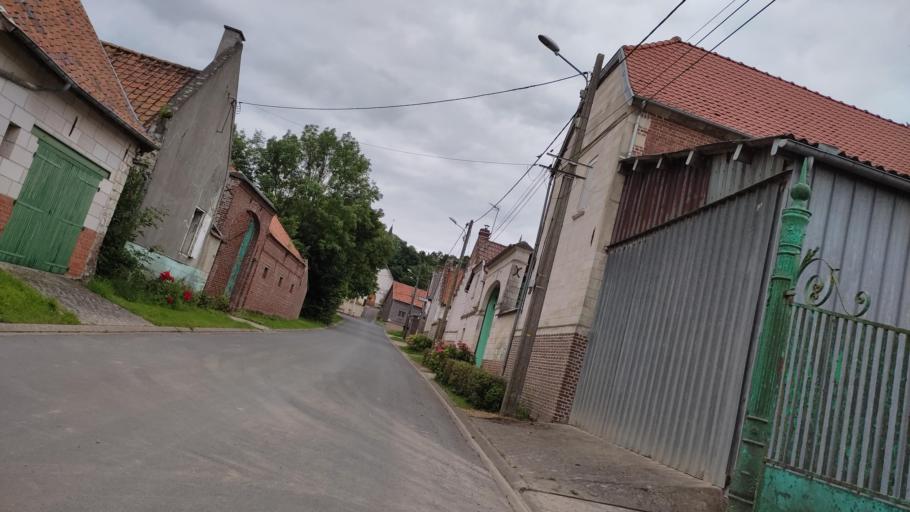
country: FR
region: Nord-Pas-de-Calais
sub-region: Departement du Pas-de-Calais
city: Beaumetz-les-Loges
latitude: 50.2401
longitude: 2.6281
